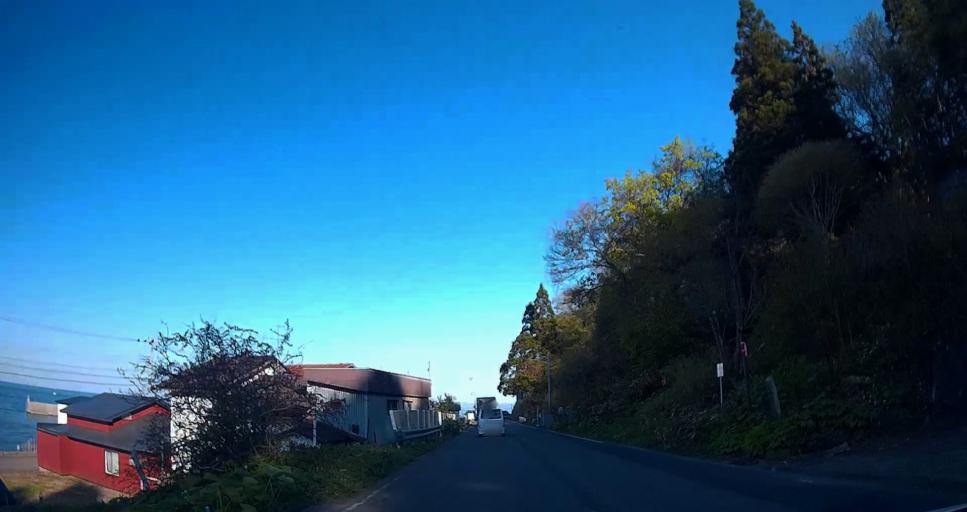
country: JP
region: Aomori
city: Mutsu
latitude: 41.4416
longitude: 141.1275
